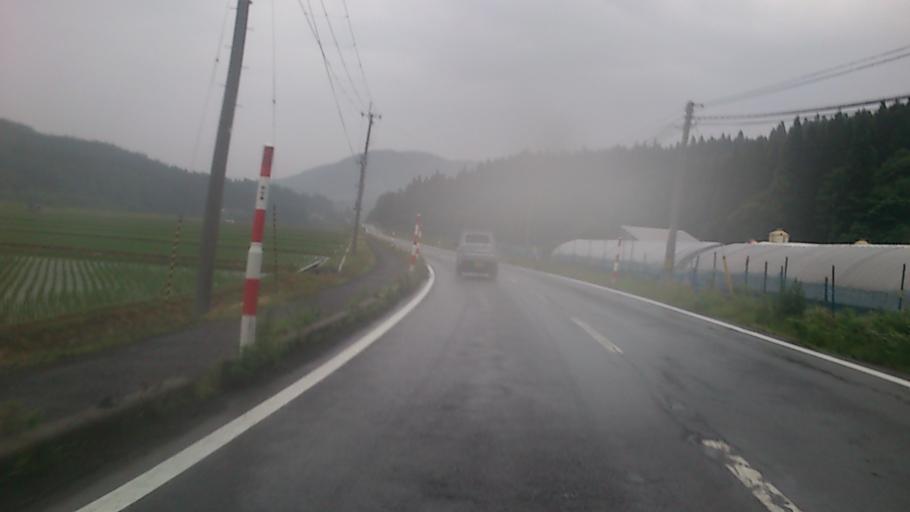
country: JP
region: Akita
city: Takanosu
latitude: 40.2908
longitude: 140.2715
